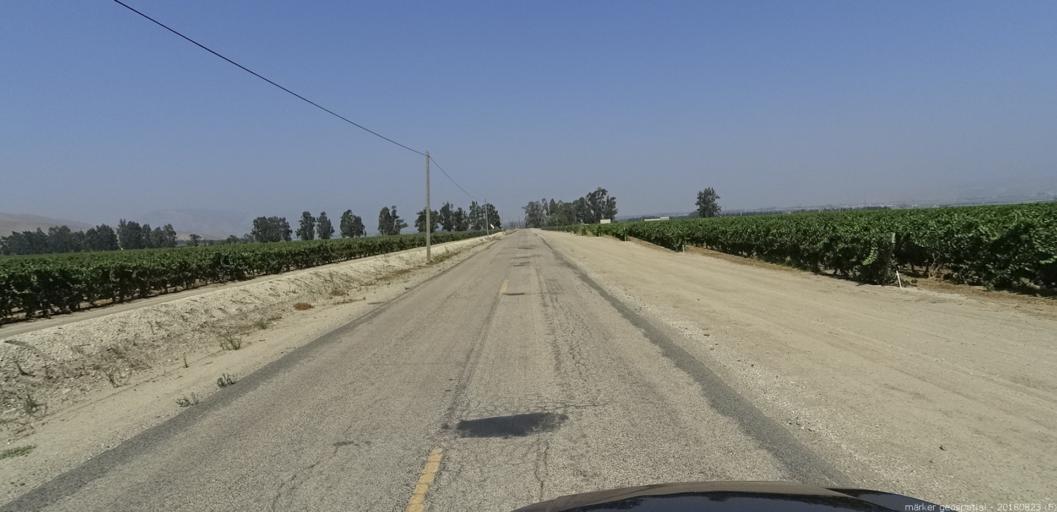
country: US
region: California
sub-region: Monterey County
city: Greenfield
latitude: 36.2738
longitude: -121.2225
